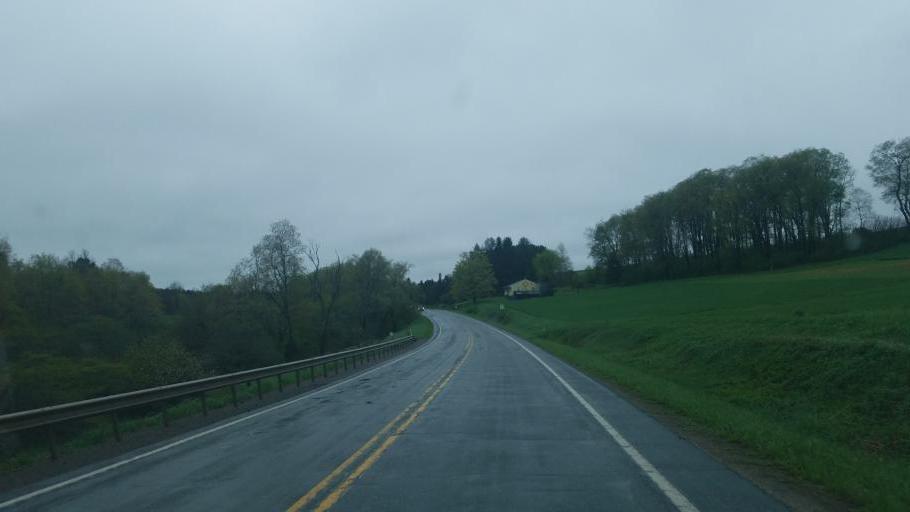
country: US
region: Pennsylvania
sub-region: Potter County
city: Coudersport
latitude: 41.8634
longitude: -77.8515
